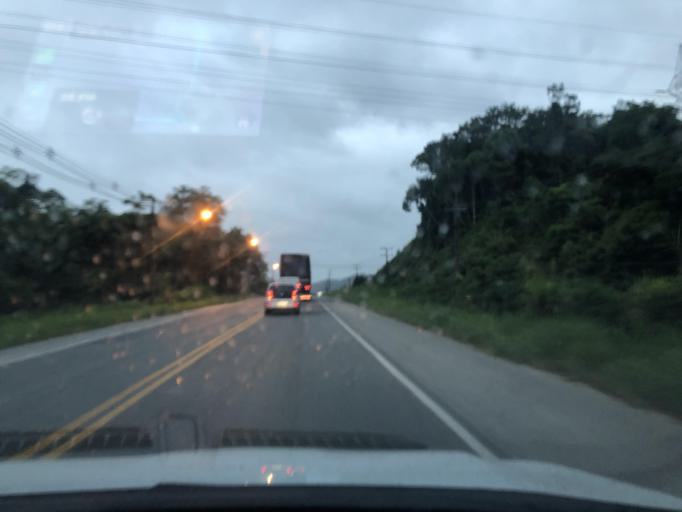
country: BR
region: Santa Catarina
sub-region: Pomerode
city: Pomerode
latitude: -26.7823
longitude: -49.0844
